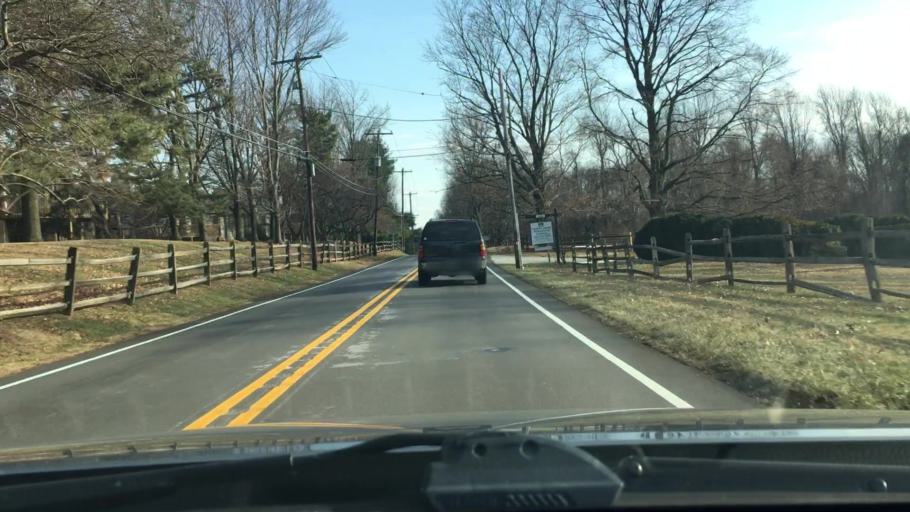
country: US
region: Pennsylvania
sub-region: Delaware County
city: Lima
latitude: 39.9646
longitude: -75.4372
